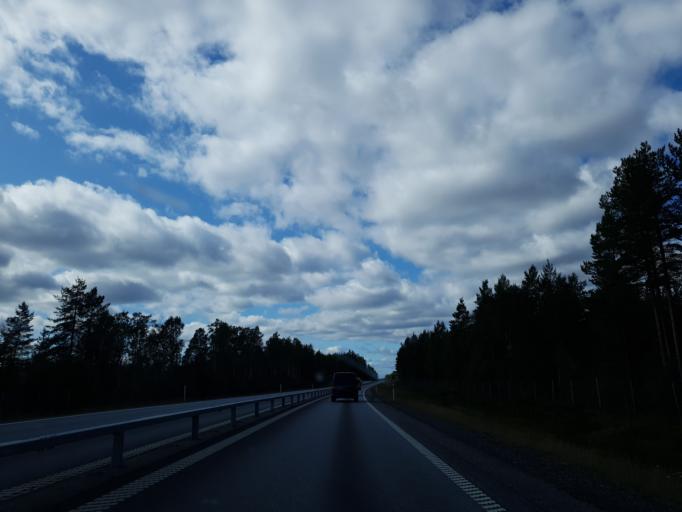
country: SE
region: Vaesterbotten
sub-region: Umea Kommun
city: Hoernefors
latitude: 63.5995
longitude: 19.7450
